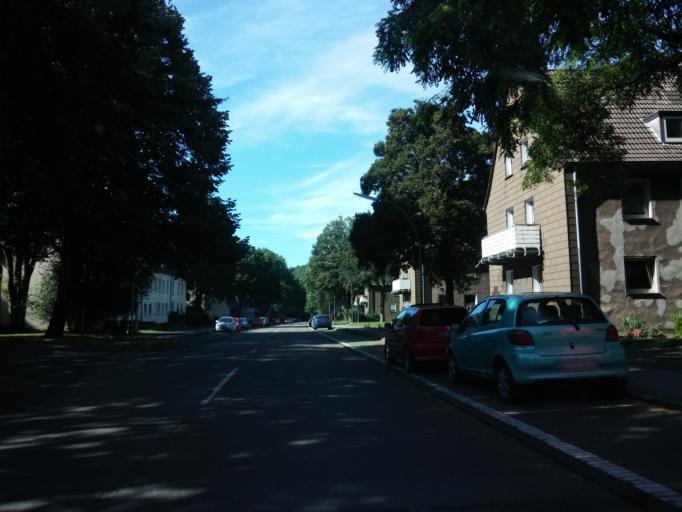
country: DE
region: North Rhine-Westphalia
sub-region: Regierungsbezirk Munster
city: Gladbeck
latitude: 51.5951
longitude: 7.0179
